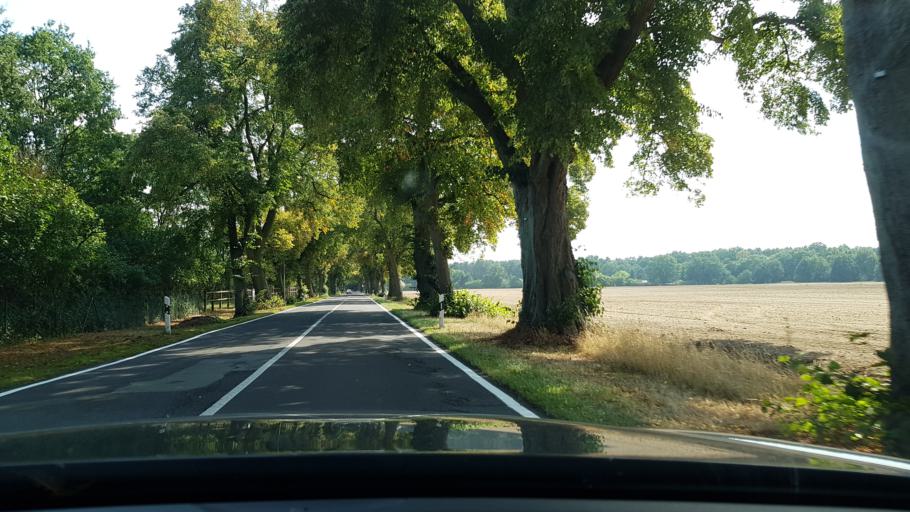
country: DE
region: Brandenburg
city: Lindow
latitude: 52.9859
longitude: 12.9783
